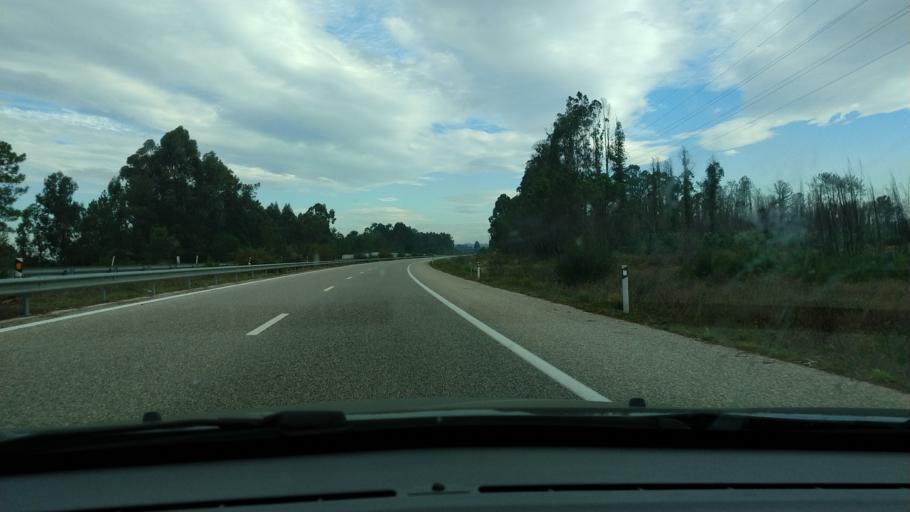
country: PT
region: Coimbra
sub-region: Mira
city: Mira
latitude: 40.4775
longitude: -8.6883
